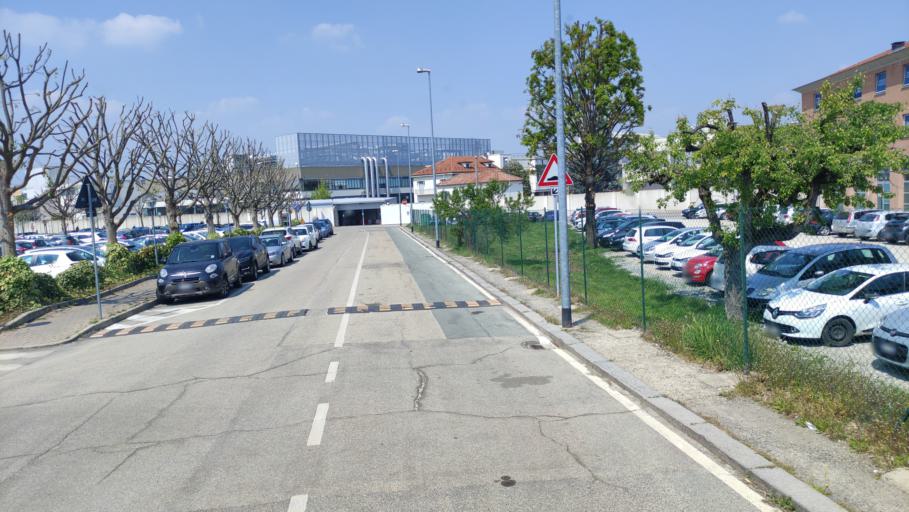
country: IT
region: Piedmont
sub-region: Provincia di Cuneo
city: Alba
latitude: 44.6978
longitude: 8.0255
